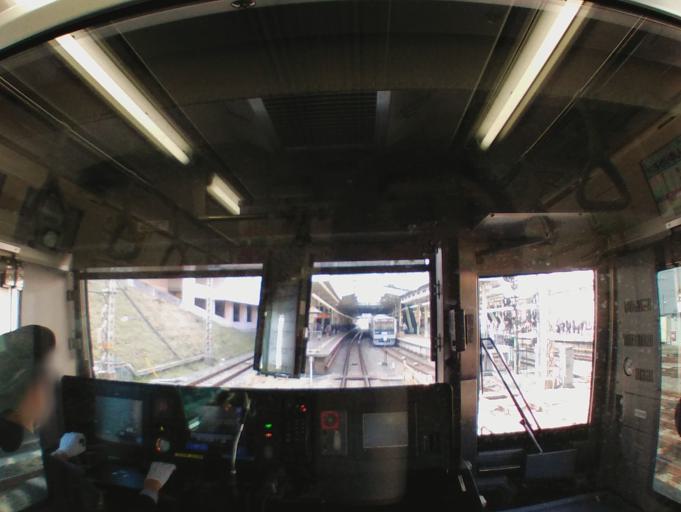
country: JP
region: Tokyo
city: Chofugaoka
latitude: 35.6056
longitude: 139.5101
